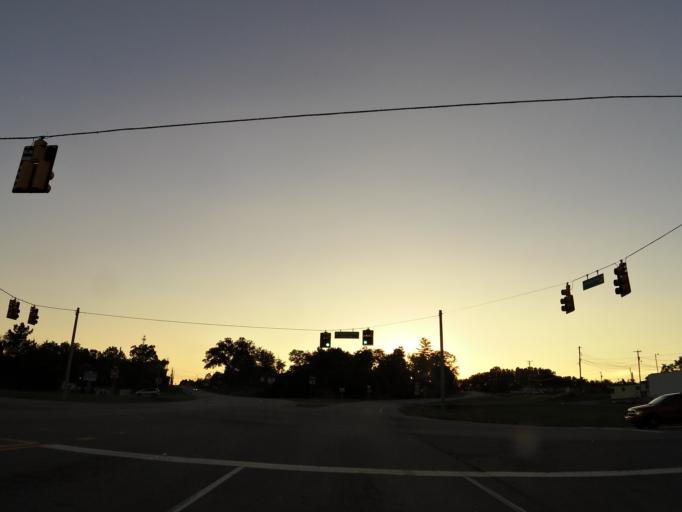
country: US
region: Tennessee
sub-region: Knox County
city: Mascot
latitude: 36.0260
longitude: -83.7295
